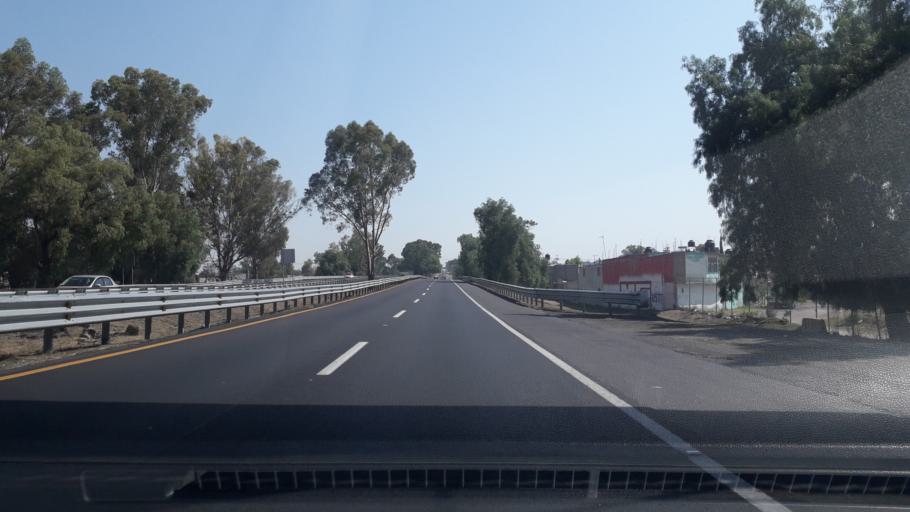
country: MX
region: Mexico
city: Santo Tomas Chiconautla
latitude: 19.6428
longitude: -99.0167
